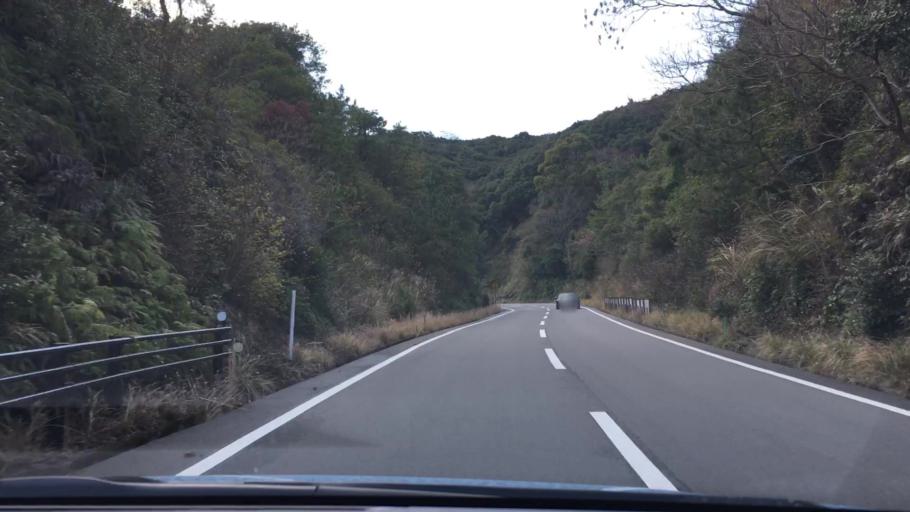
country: JP
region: Mie
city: Toba
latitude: 34.4327
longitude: 136.9127
